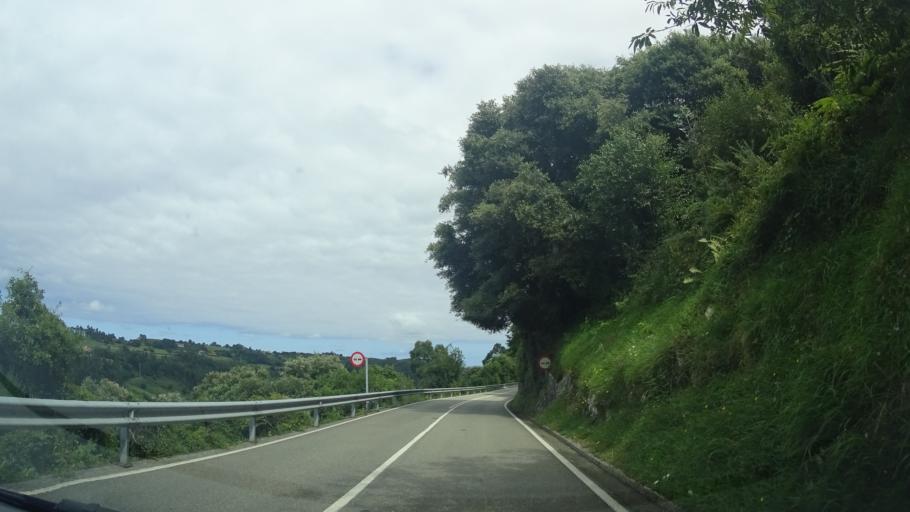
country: ES
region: Asturias
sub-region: Province of Asturias
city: Ribadesella
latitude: 43.4642
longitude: -5.1008
